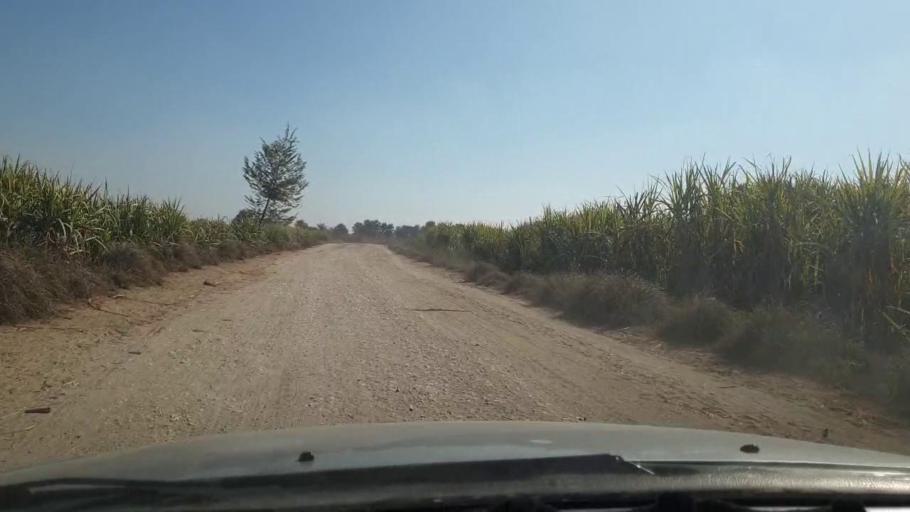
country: PK
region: Sindh
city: Ghotki
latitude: 28.0247
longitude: 69.2197
